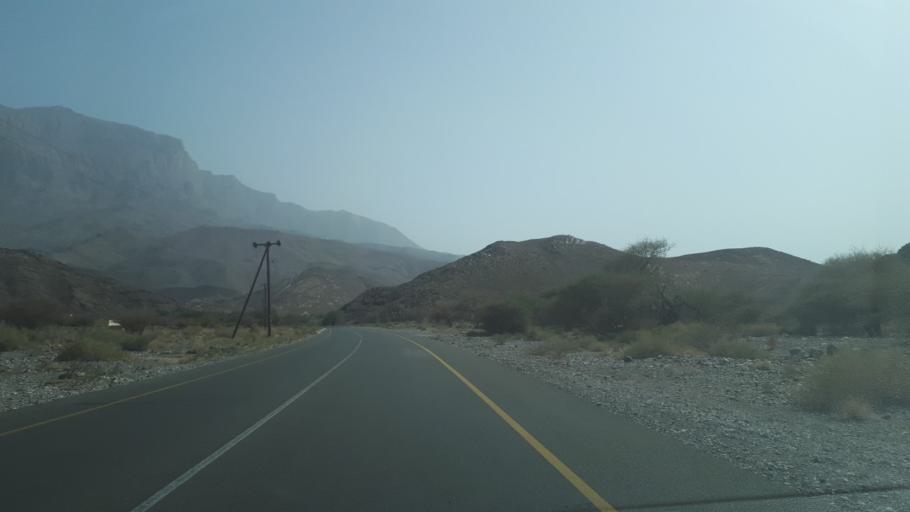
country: OM
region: Muhafazat ad Dakhiliyah
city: Bahla'
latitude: 23.2185
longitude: 57.0276
